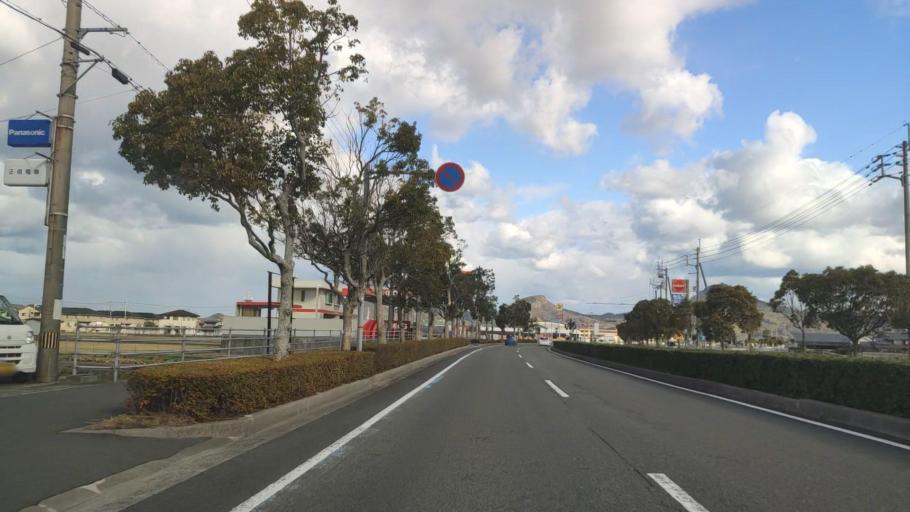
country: JP
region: Ehime
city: Hojo
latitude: 33.9653
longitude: 132.7789
